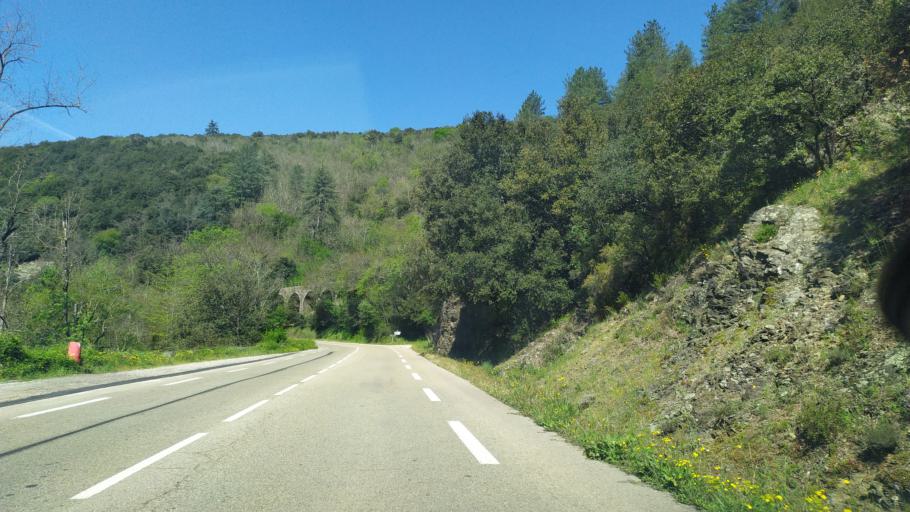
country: FR
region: Languedoc-Roussillon
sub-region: Departement du Gard
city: Le Vigan
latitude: 43.9973
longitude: 3.6446
